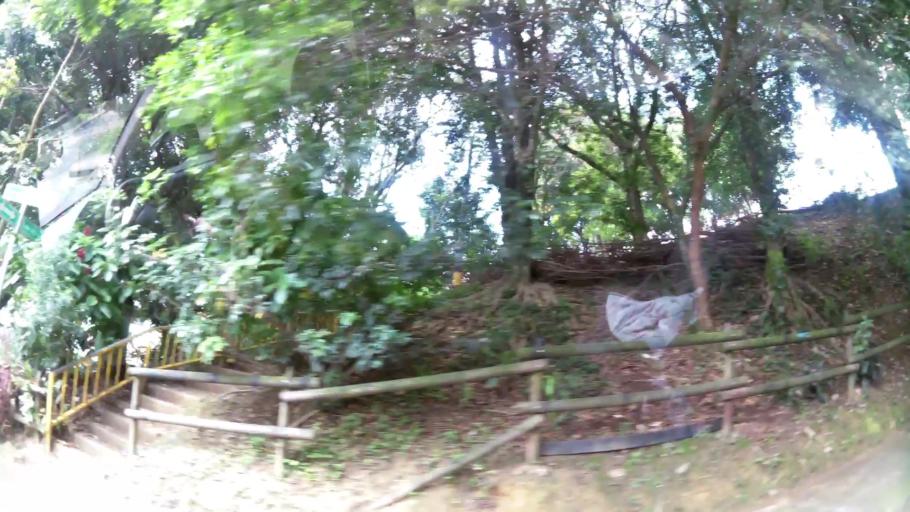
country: CO
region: Antioquia
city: La Estrella
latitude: 6.1776
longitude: -75.6401
